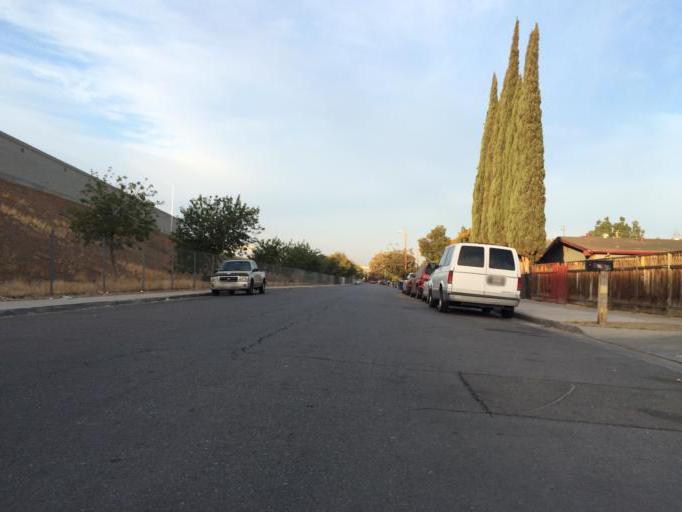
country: US
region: California
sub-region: Fresno County
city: Fresno
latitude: 36.7559
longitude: -119.7687
